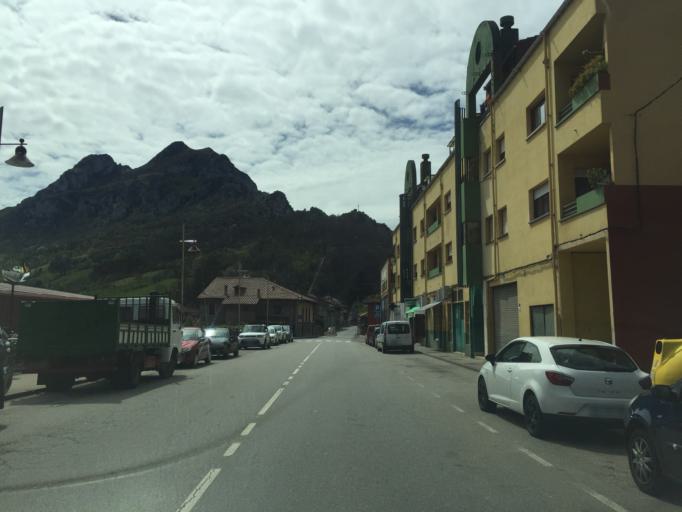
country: ES
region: Asturias
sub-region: Province of Asturias
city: Proaza
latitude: 43.2536
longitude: -6.0146
